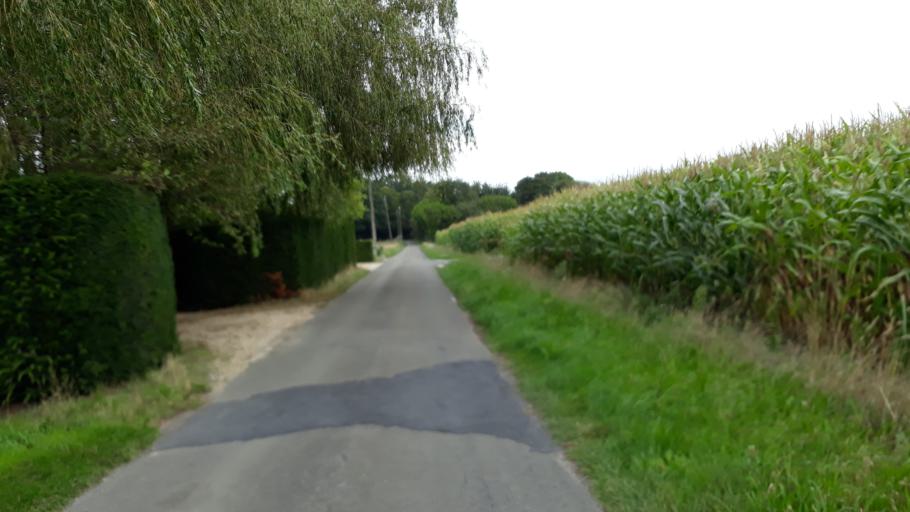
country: BE
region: Flanders
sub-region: Provincie West-Vlaanderen
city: Torhout
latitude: 51.0584
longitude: 3.1309
